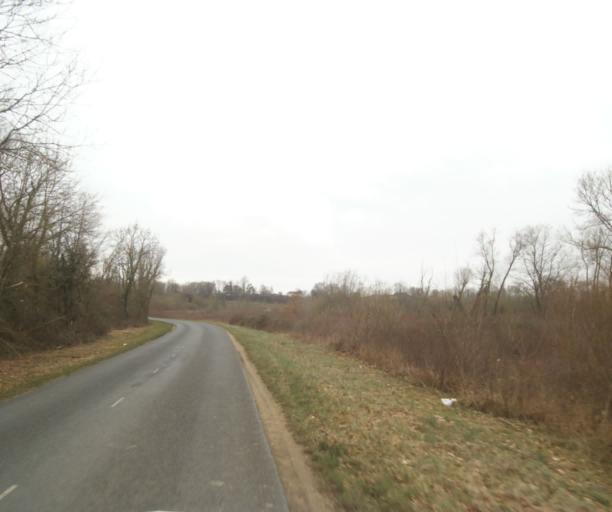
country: FR
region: Champagne-Ardenne
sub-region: Departement de la Haute-Marne
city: Villiers-en-Lieu
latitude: 48.6395
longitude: 4.8380
